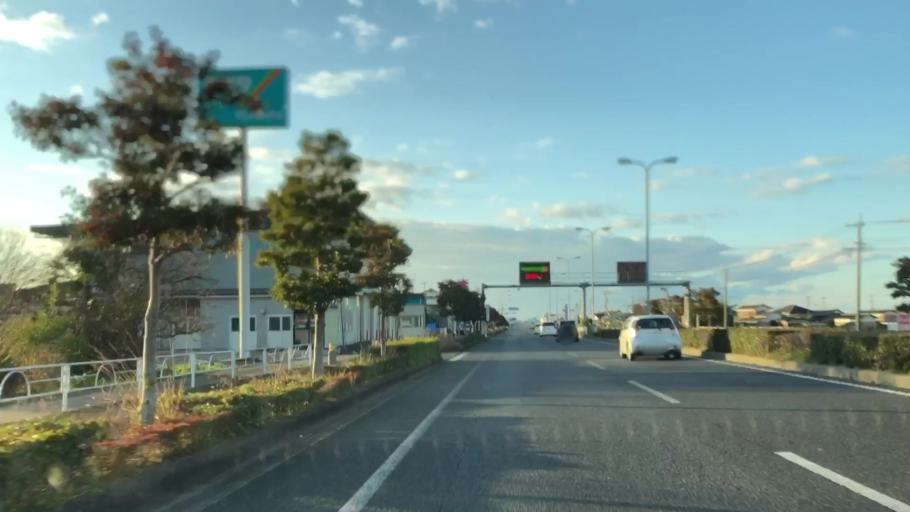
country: JP
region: Fukuoka
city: Nakatsu
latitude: 33.5455
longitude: 131.2839
